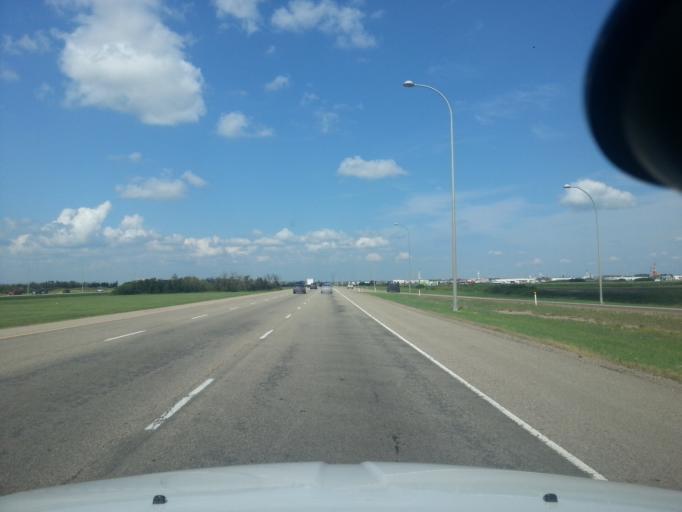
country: CA
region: Alberta
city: Leduc
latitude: 53.3131
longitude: -113.5479
